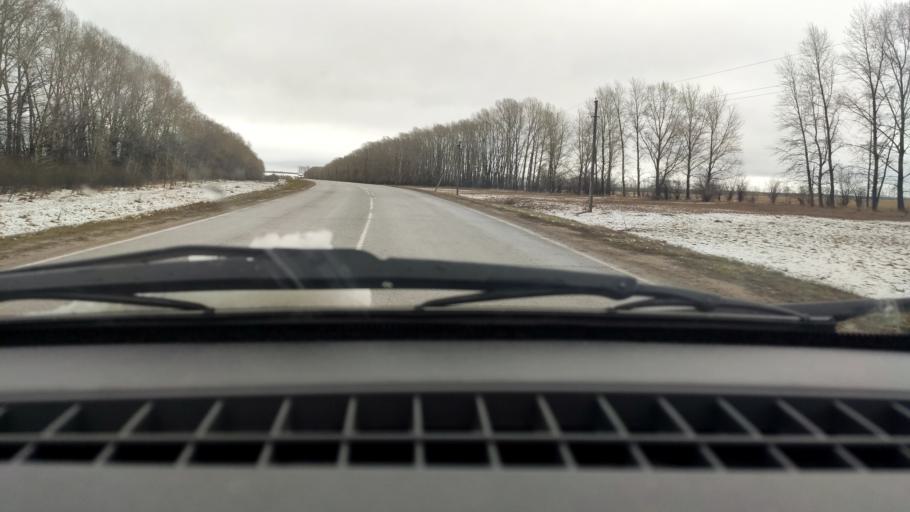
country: RU
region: Bashkortostan
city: Alekseyevka
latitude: 55.0643
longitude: 55.0975
